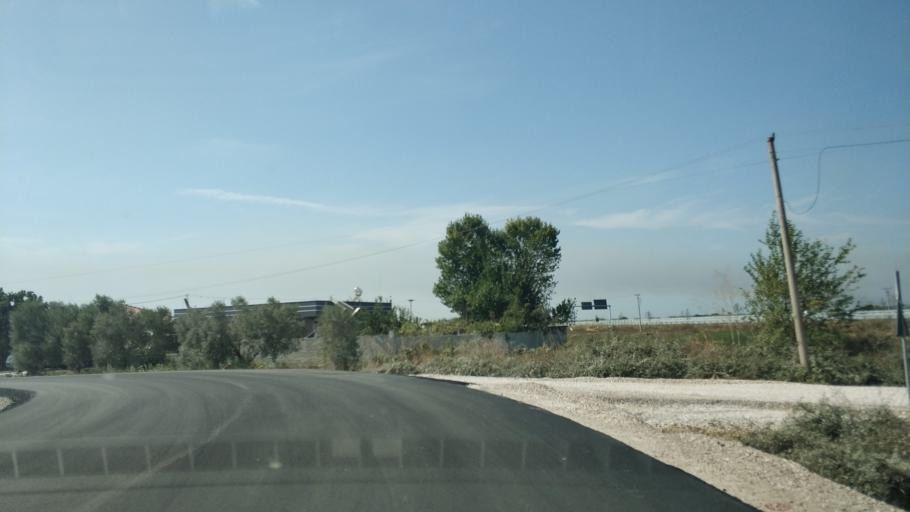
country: AL
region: Fier
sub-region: Rrethi i Fierit
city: Dermenas
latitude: 40.7402
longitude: 19.4801
